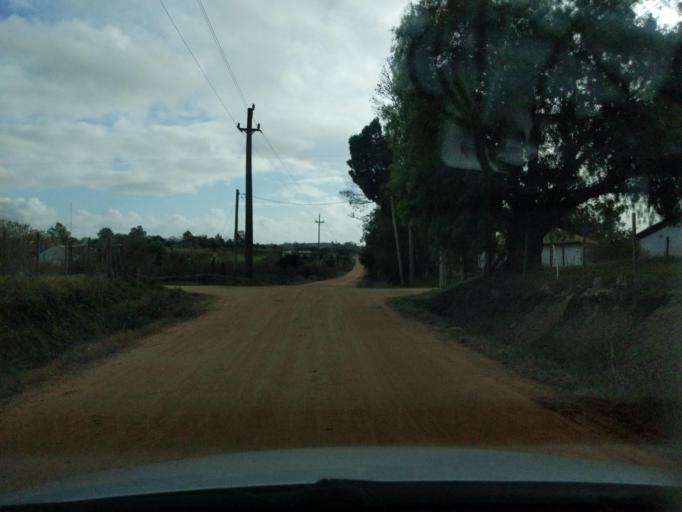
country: UY
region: Florida
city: Florida
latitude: -34.0689
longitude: -56.2199
